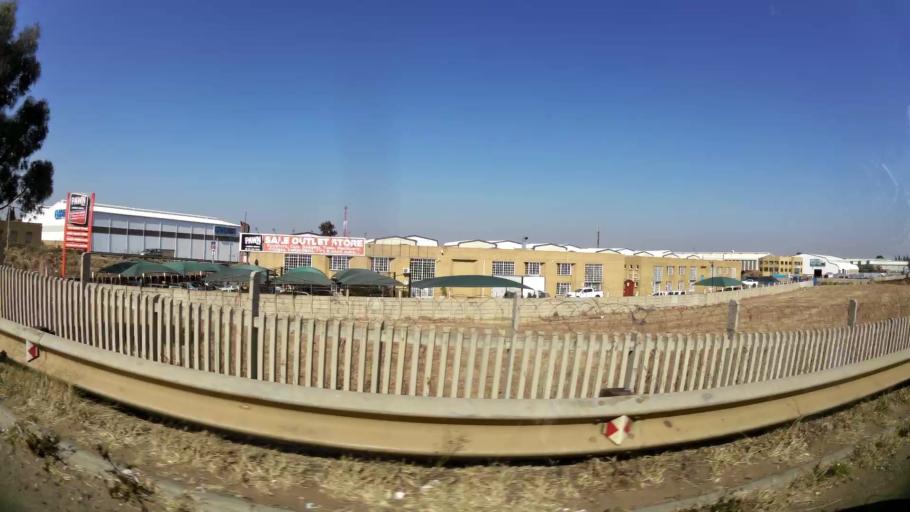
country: ZA
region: Gauteng
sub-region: Ekurhuleni Metropolitan Municipality
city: Boksburg
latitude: -26.1548
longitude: 28.2198
